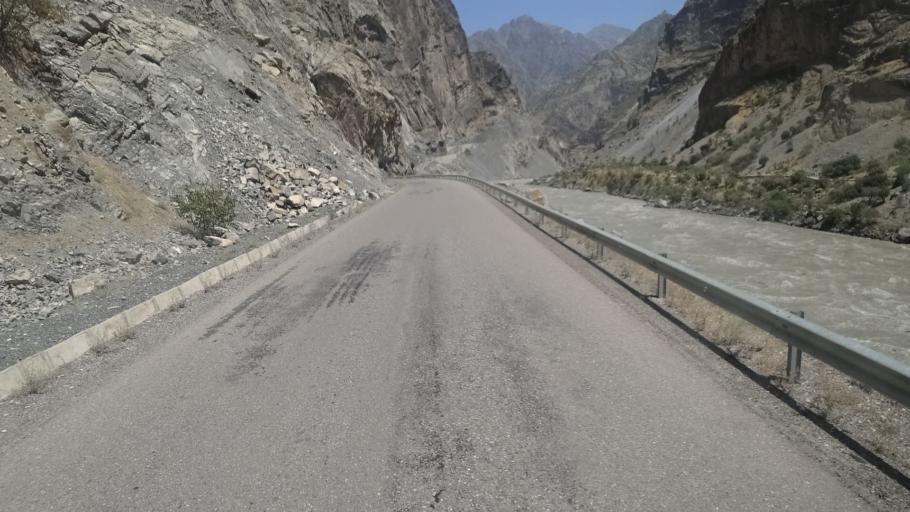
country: AF
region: Badakhshan
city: Deh Khwahan
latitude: 37.9970
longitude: 70.3099
